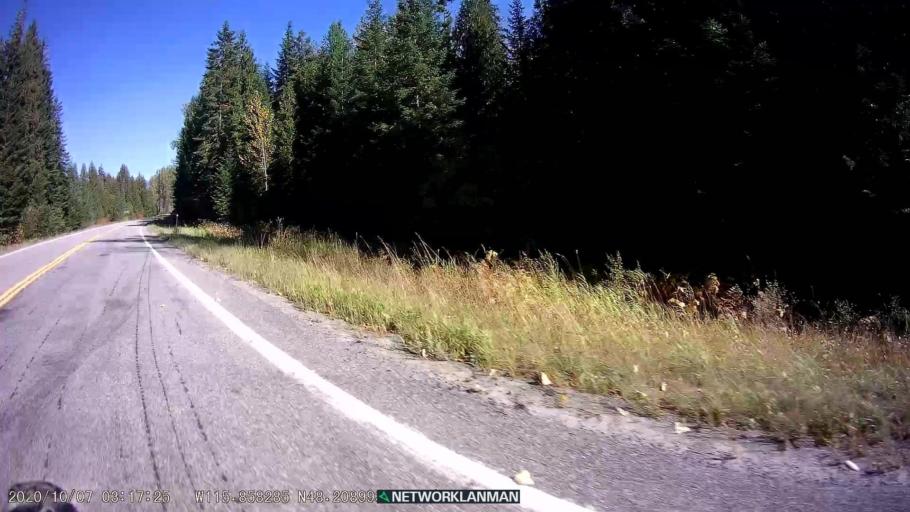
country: US
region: Montana
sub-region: Lincoln County
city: Libby
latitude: 48.2093
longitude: -115.8583
